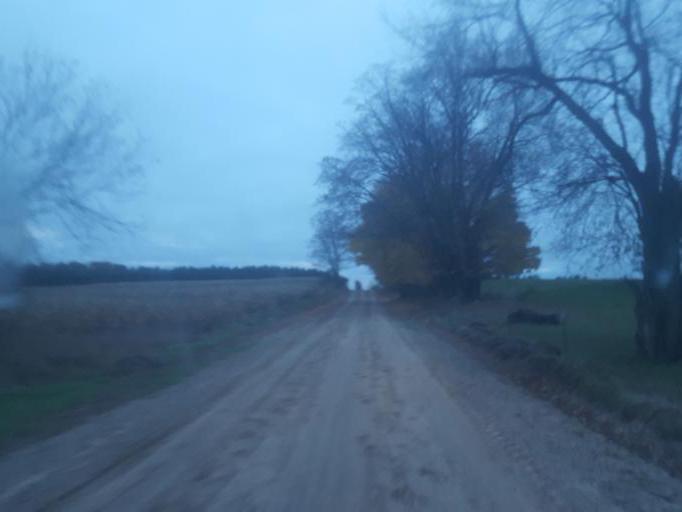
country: US
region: Michigan
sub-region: Isabella County
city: Lake Isabella
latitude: 43.5410
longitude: -85.0658
